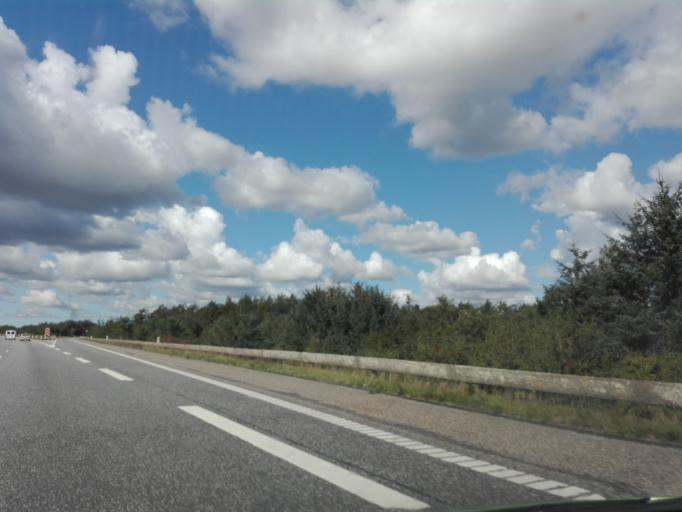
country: DK
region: North Denmark
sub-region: Mariagerfjord Kommune
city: Hobro
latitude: 56.5683
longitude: 9.8561
